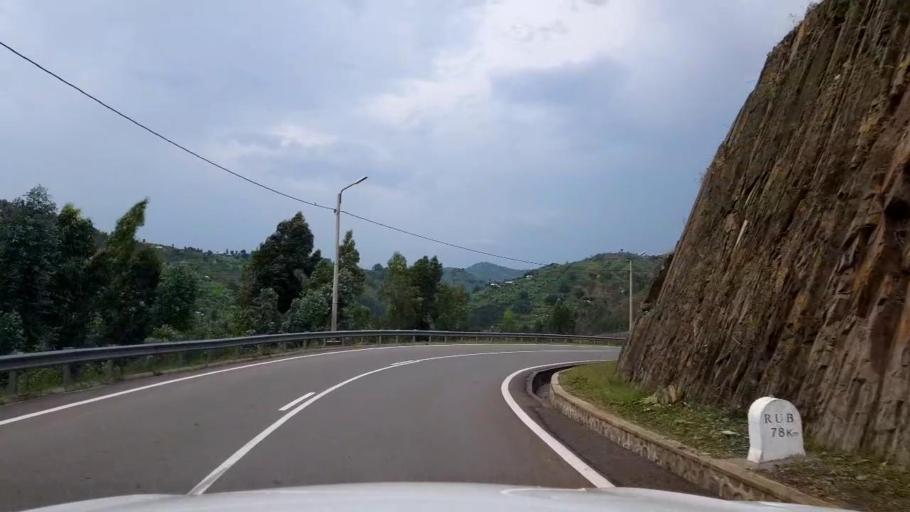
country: RW
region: Western Province
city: Kibuye
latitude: -2.0358
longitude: 29.3981
